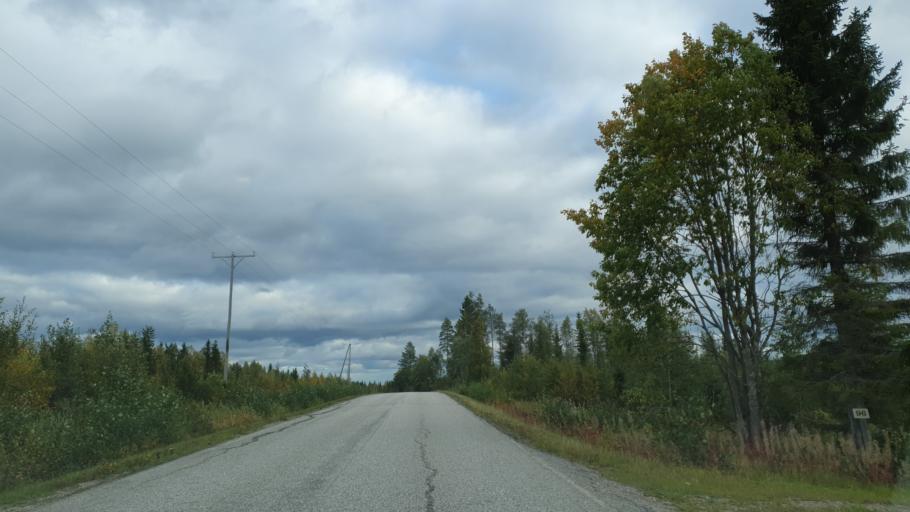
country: FI
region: Kainuu
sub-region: Kehys-Kainuu
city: Kuhmo
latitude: 63.9540
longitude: 29.7374
